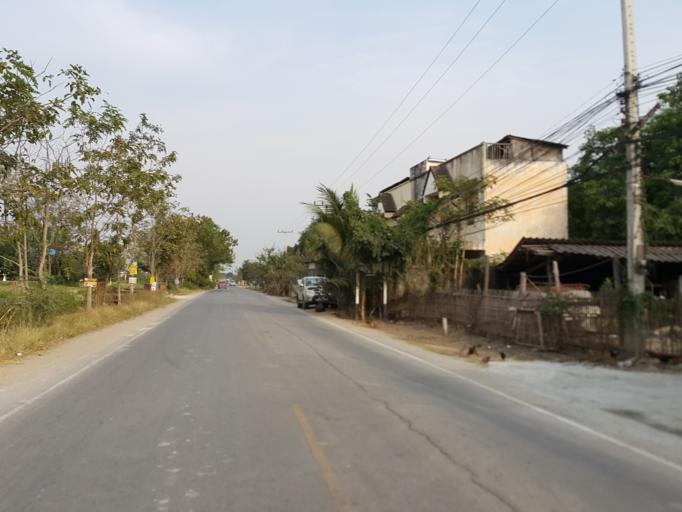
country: TH
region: Chiang Mai
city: Hang Dong
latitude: 18.6895
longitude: 98.9478
